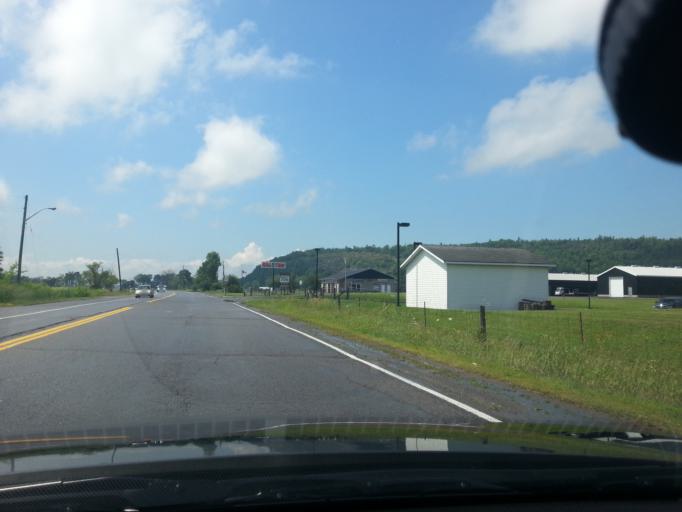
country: CA
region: Ontario
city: Renfrew
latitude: 45.4823
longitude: -76.7033
